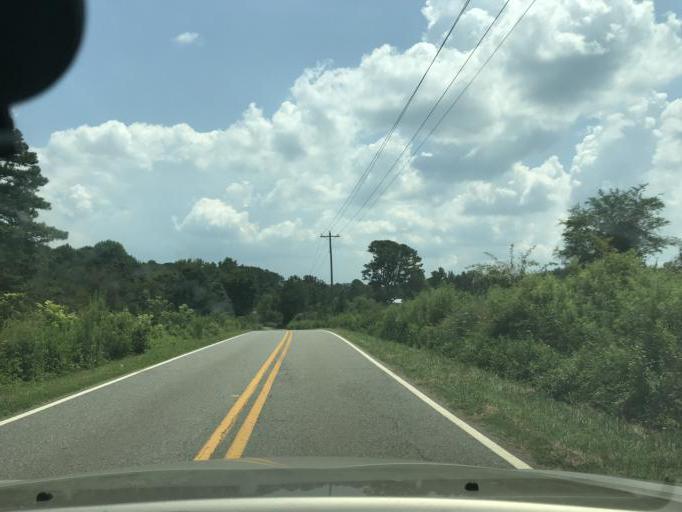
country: US
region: Georgia
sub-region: Forsyth County
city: Cumming
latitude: 34.2658
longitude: -84.1553
